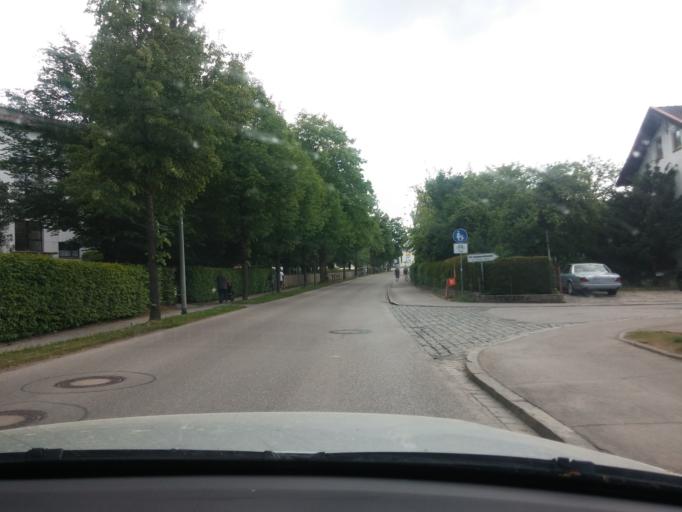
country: DE
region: Bavaria
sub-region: Upper Bavaria
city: Holzkirchen
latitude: 47.8840
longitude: 11.7062
